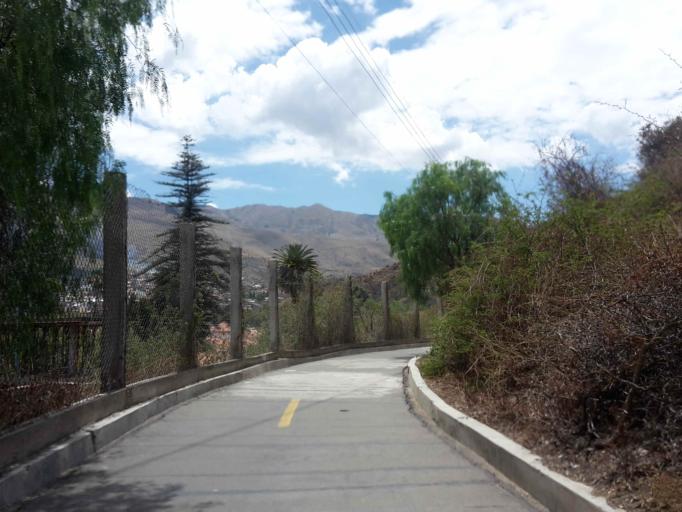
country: BO
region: Cochabamba
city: Cochabamba
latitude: -17.3812
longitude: -66.1412
